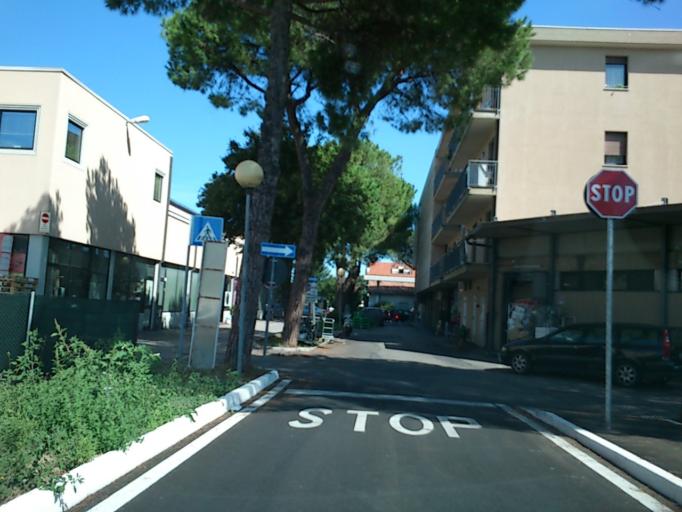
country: IT
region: Emilia-Romagna
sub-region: Provincia di Rimini
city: Cattolica
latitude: 43.9553
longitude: 12.7313
